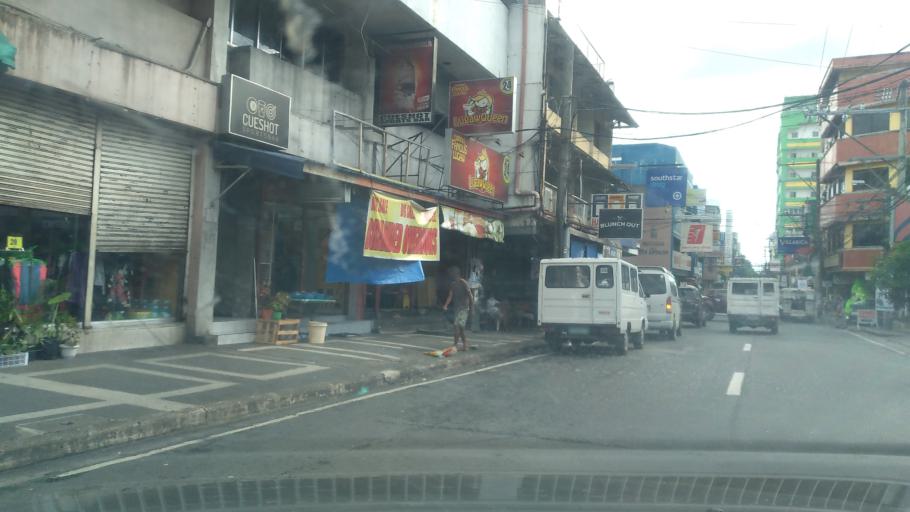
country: PH
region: Calabarzon
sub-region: Province of Quezon
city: Lucena
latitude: 13.9337
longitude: 121.6129
